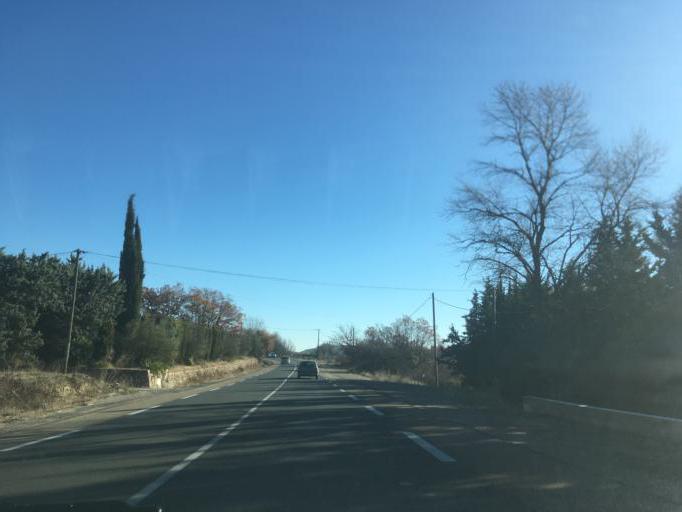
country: FR
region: Provence-Alpes-Cote d'Azur
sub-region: Departement du Var
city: Flayosc
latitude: 43.5294
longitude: 6.4186
